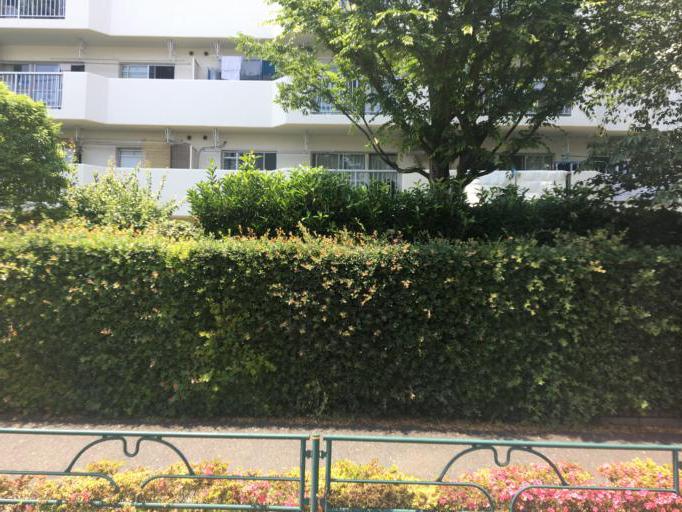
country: JP
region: Saitama
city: Shimotoda
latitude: 35.7647
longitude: 139.6845
